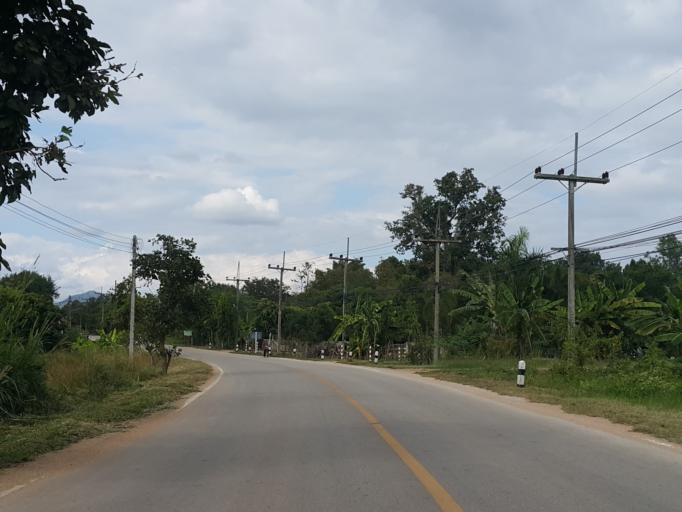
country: TH
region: Lampang
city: Chae Hom
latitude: 18.5678
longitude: 99.4726
